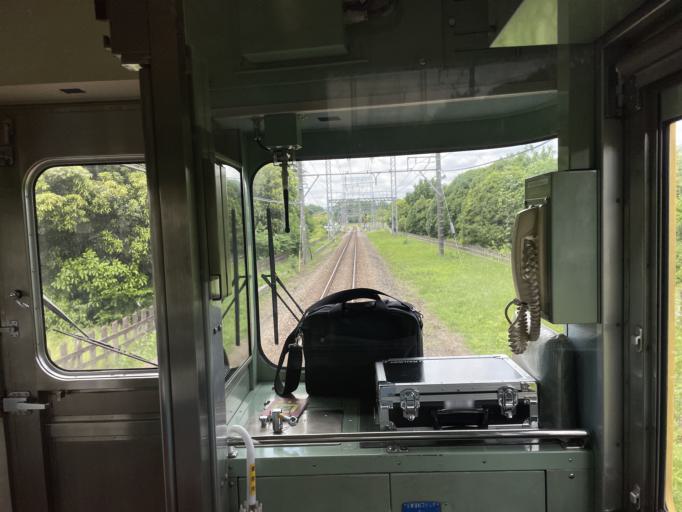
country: JP
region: Tokyo
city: Fussa
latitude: 35.7247
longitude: 139.3608
